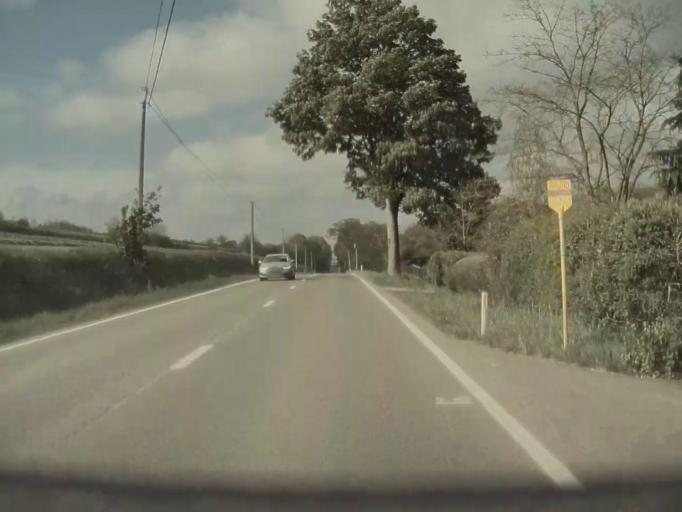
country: BE
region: Wallonia
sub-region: Province de Namur
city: Somme-Leuze
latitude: 50.3269
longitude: 5.3551
